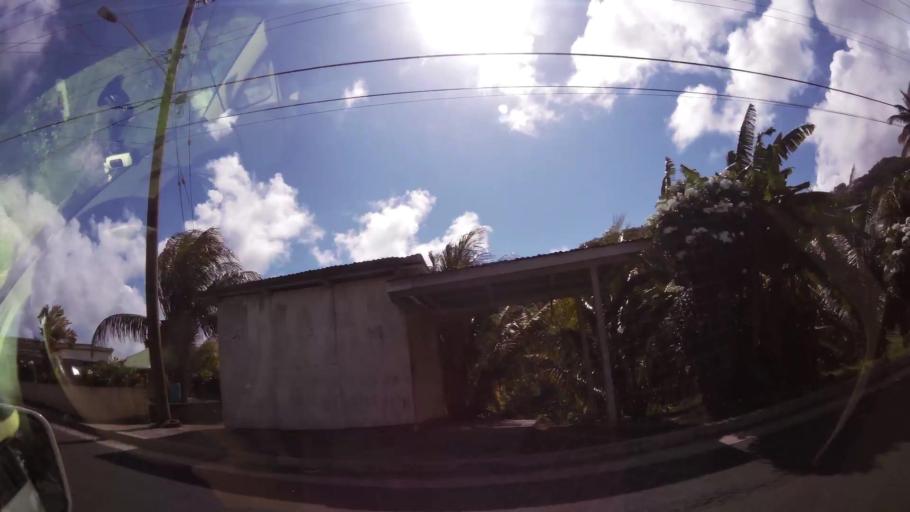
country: VC
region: Saint George
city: Kingstown
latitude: 13.1438
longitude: -61.1761
